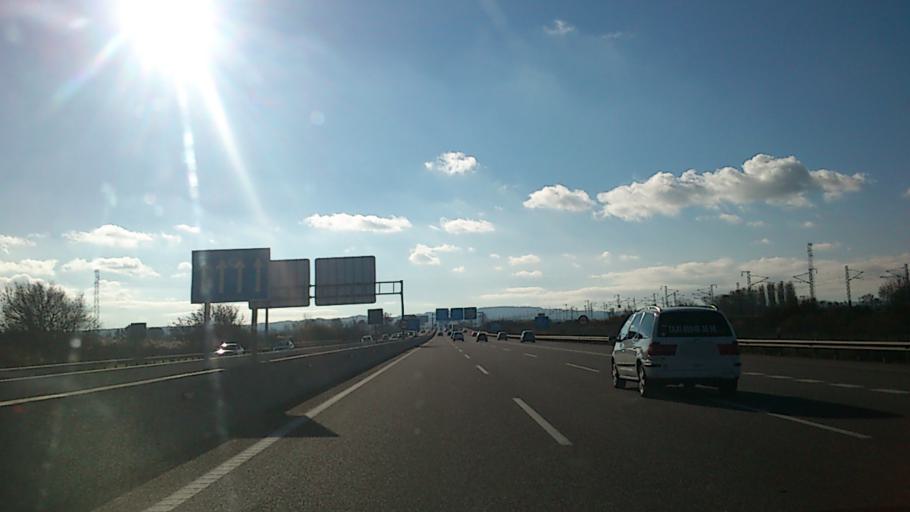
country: ES
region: Aragon
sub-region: Provincia de Zaragoza
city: Oliver-Valdefierro, Oliver, Valdefierro
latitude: 41.6527
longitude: -0.9591
